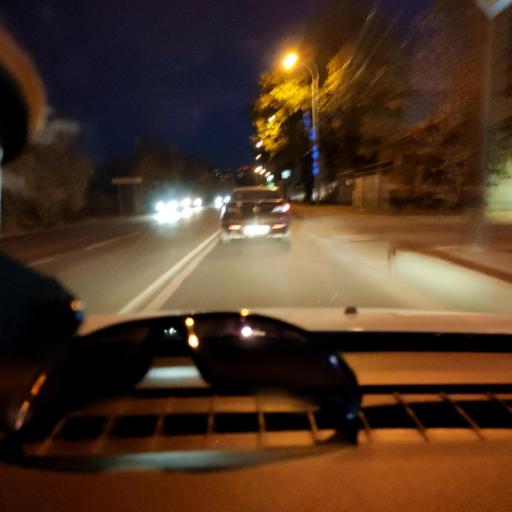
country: RU
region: Samara
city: Rozhdestveno
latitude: 53.1648
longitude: 50.0761
